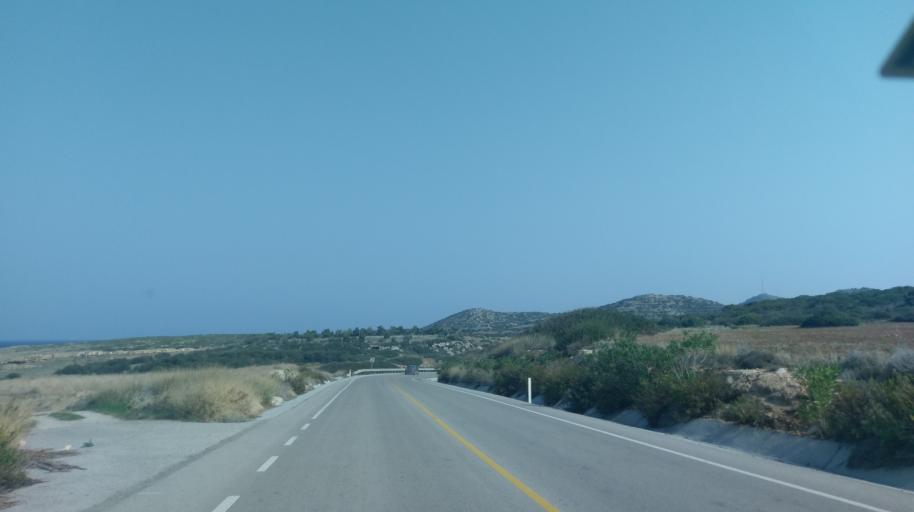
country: CY
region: Ammochostos
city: Leonarisso
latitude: 35.4852
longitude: 34.0721
